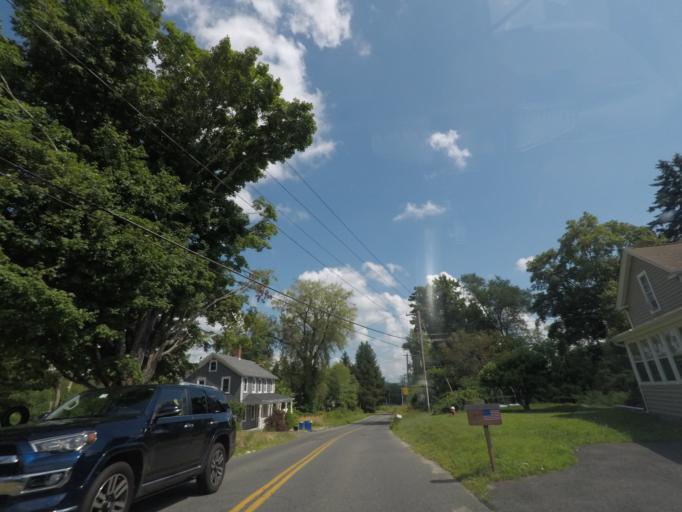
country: US
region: Massachusetts
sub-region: Hampden County
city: Monson
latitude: 42.1158
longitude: -72.3295
